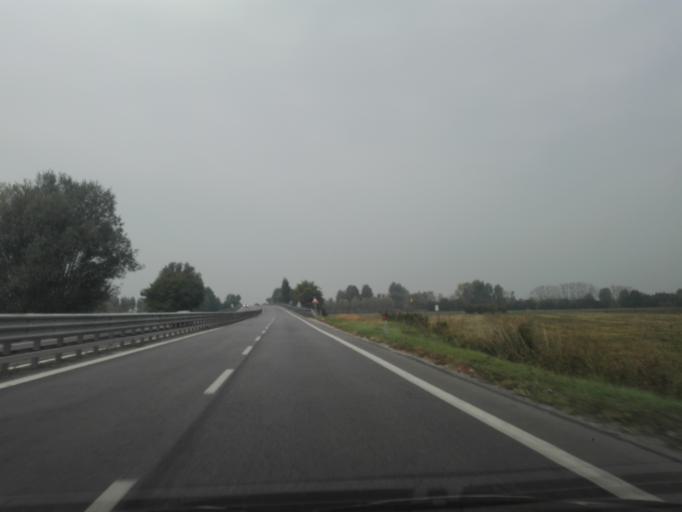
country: IT
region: Veneto
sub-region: Provincia di Verona
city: Legnago
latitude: 45.1727
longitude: 11.2901
